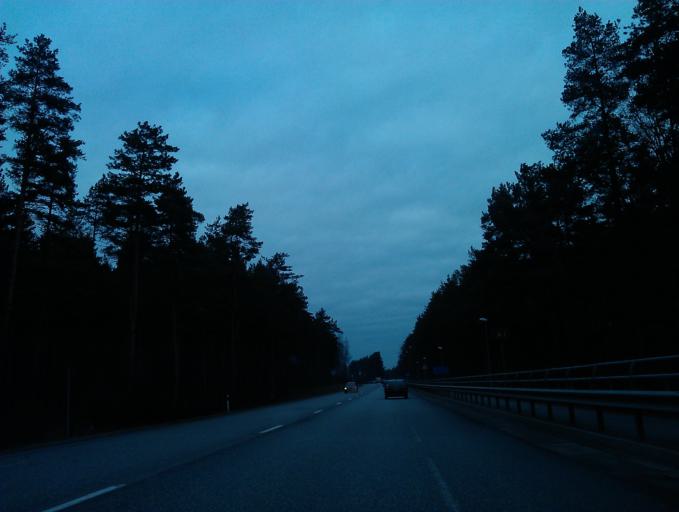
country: LV
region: Adazi
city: Adazi
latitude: 57.0556
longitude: 24.3209
